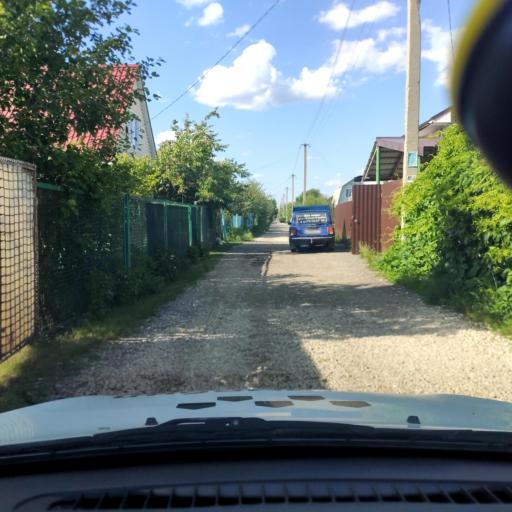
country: RU
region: Samara
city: Tol'yatti
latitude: 53.5940
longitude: 49.2928
